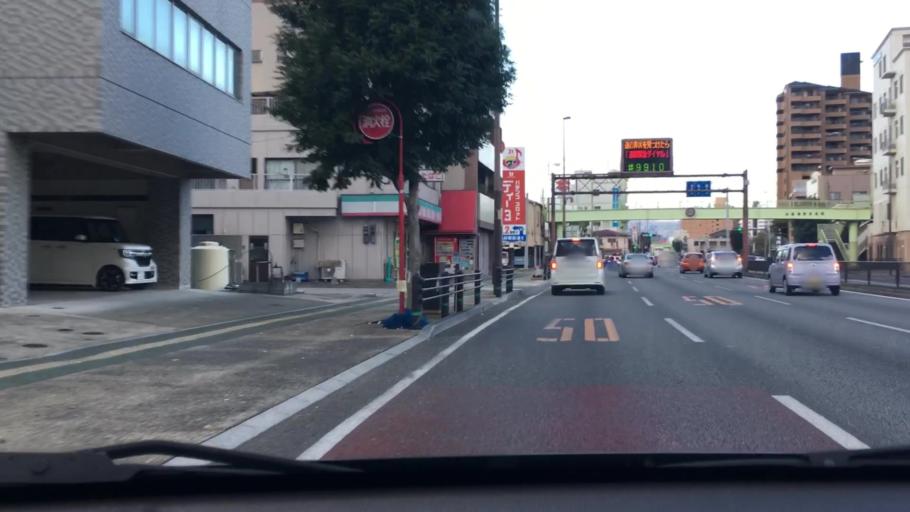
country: JP
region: Oita
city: Beppu
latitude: 33.2686
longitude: 131.5105
